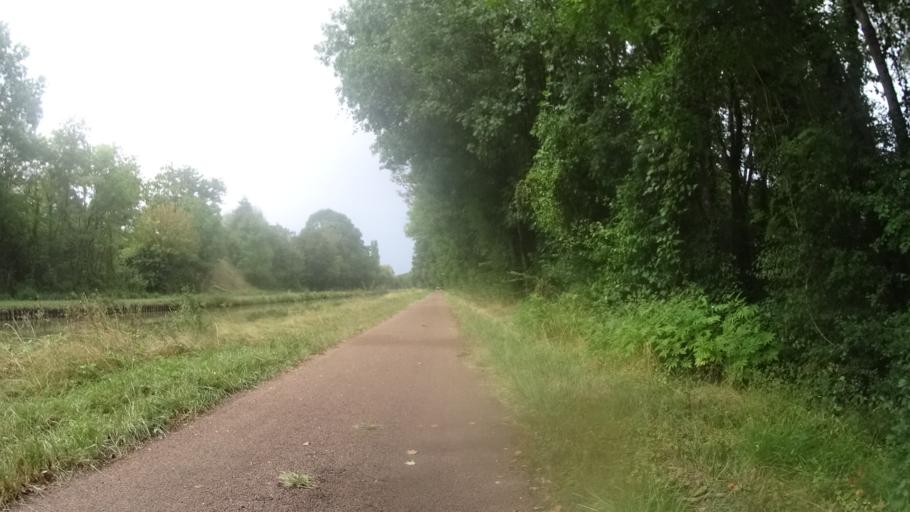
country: FR
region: Bourgogne
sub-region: Departement de la Nievre
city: Imphy
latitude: 46.9184
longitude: 3.2410
